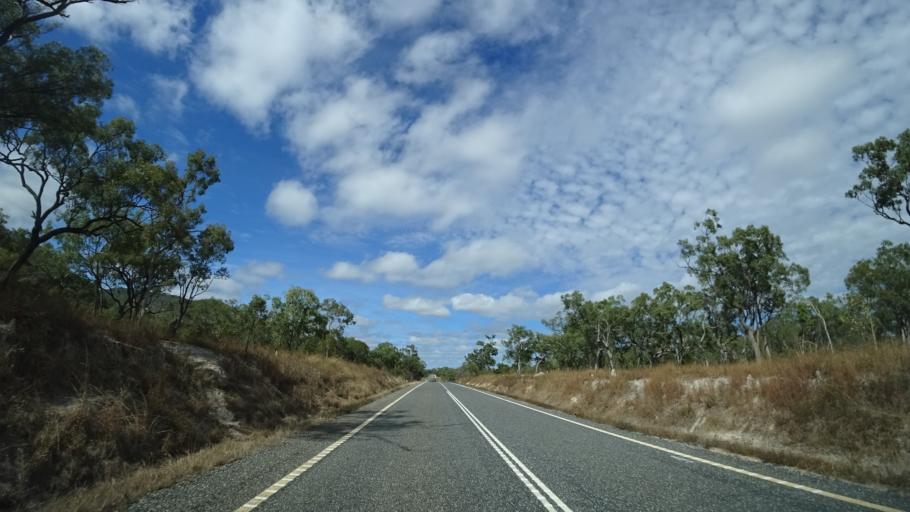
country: AU
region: Queensland
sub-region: Cairns
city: Port Douglas
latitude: -16.3280
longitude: 144.7210
